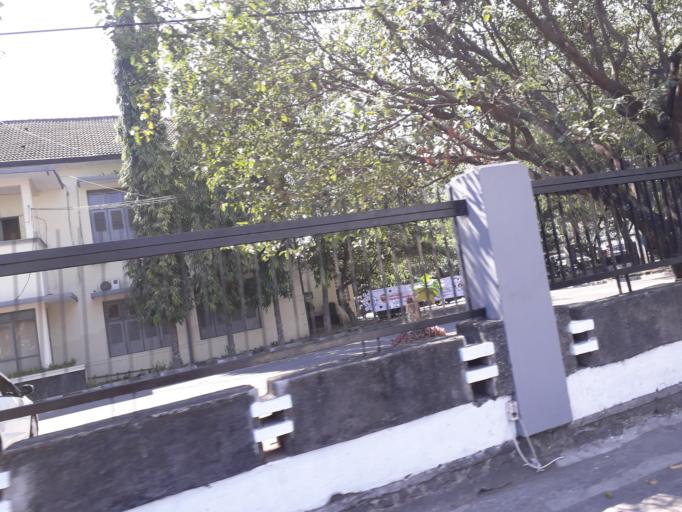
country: ID
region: Daerah Istimewa Yogyakarta
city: Yogyakarta
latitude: -7.7742
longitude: 110.3752
